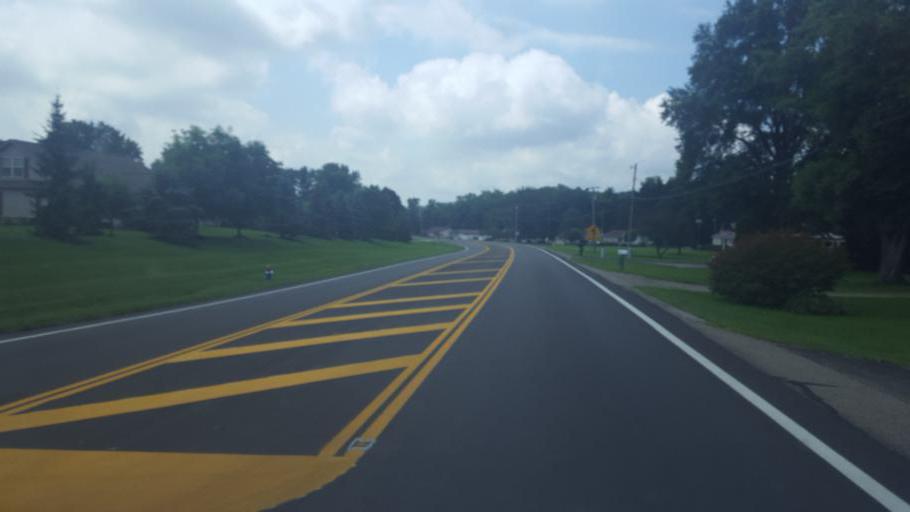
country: US
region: Ohio
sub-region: Fairfield County
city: Lancaster
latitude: 39.7504
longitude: -82.5850
